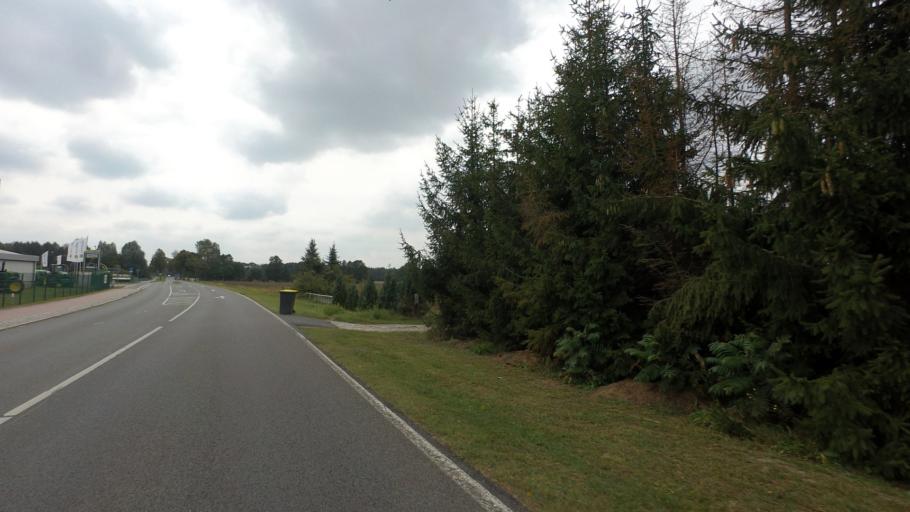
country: DE
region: Brandenburg
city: Sonnewalde
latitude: 51.6780
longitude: 13.6439
